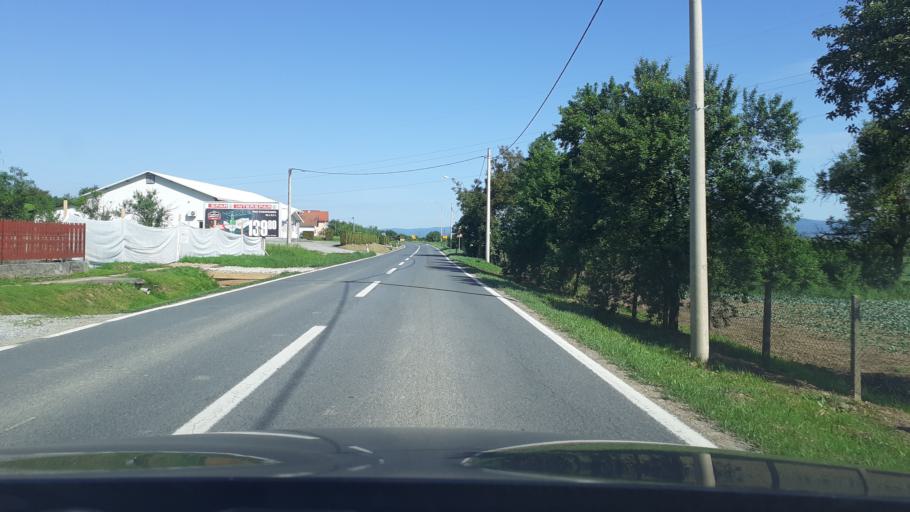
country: HR
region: Pozesko-Slavonska
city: Jaksic
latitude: 45.3182
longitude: 17.7736
